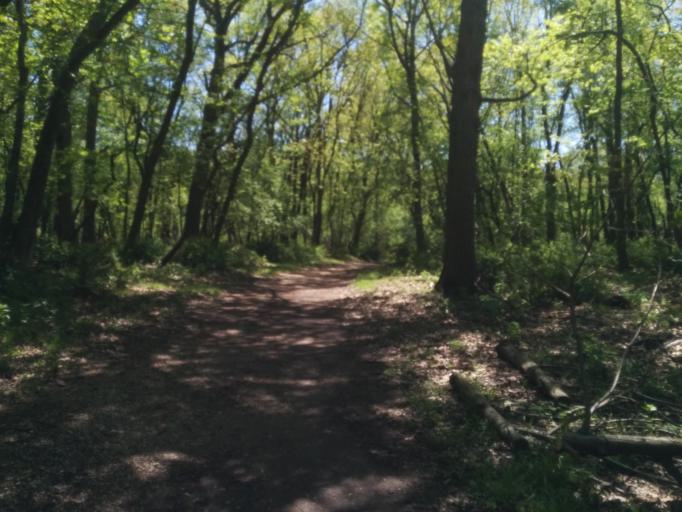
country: US
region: Illinois
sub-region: Cook County
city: Schiller Park
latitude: 41.9763
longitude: -87.8573
